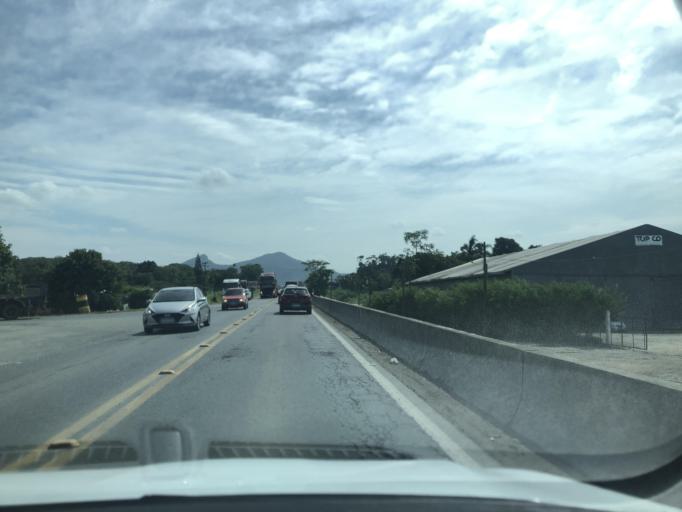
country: BR
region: Santa Catarina
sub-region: Sao Francisco Do Sul
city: Sao Francisco do Sul
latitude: -26.2639
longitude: -48.6310
